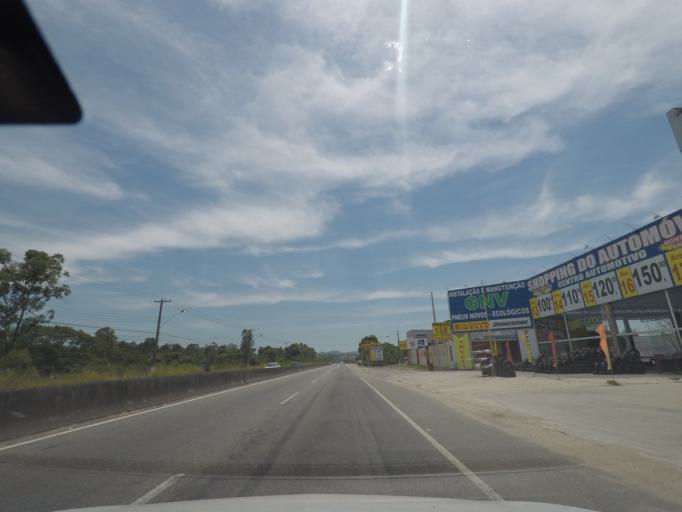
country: BR
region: Rio de Janeiro
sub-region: Marica
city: Marica
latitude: -22.9189
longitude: -42.8536
